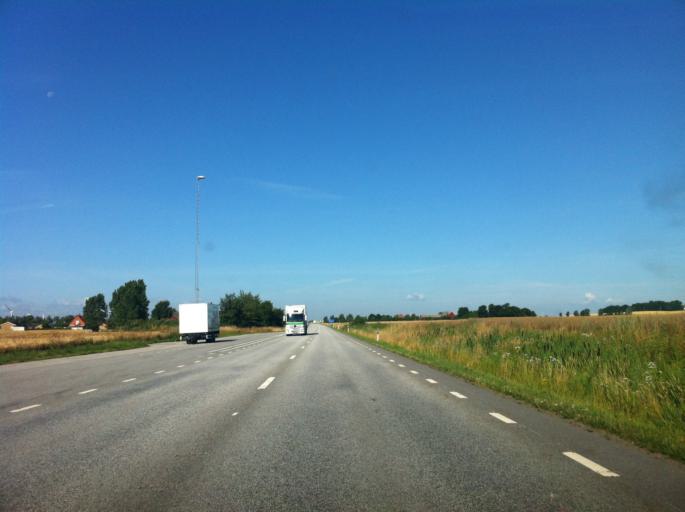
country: SE
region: Skane
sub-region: Landskrona
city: Asmundtorp
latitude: 55.8909
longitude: 12.9538
